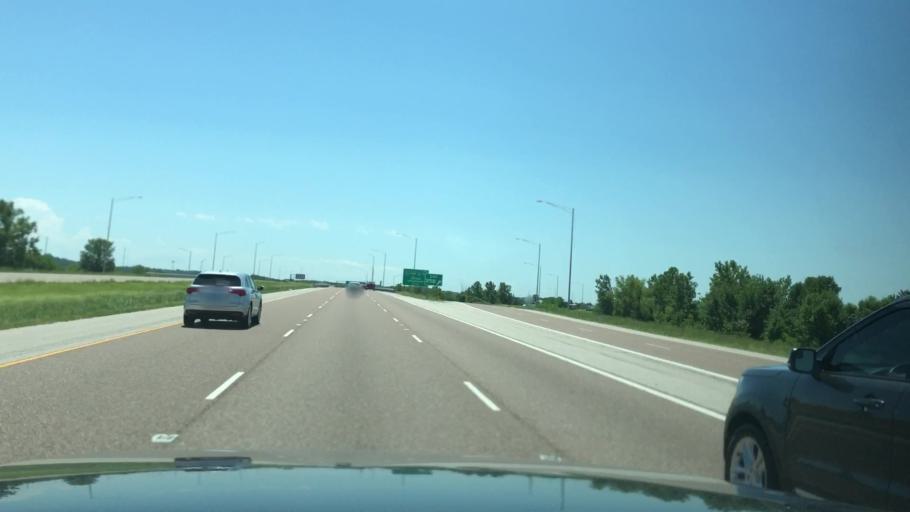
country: US
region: Illinois
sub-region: Saint Clair County
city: Caseyville
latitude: 38.6795
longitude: -90.0302
